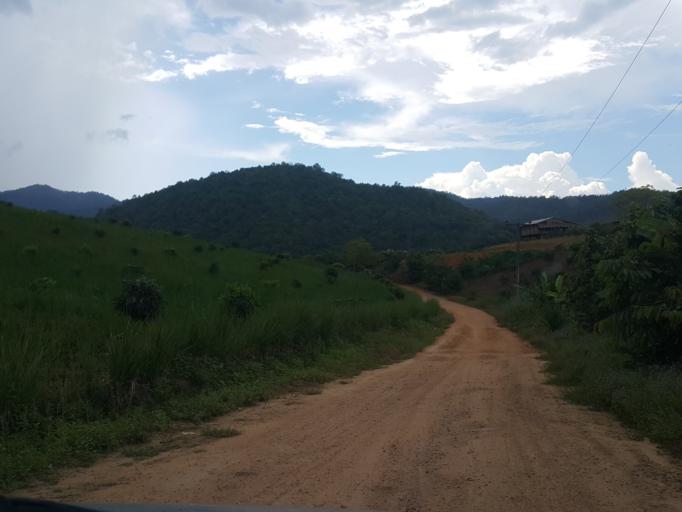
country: TH
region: Chiang Mai
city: Phrao
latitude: 19.3293
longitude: 99.1373
